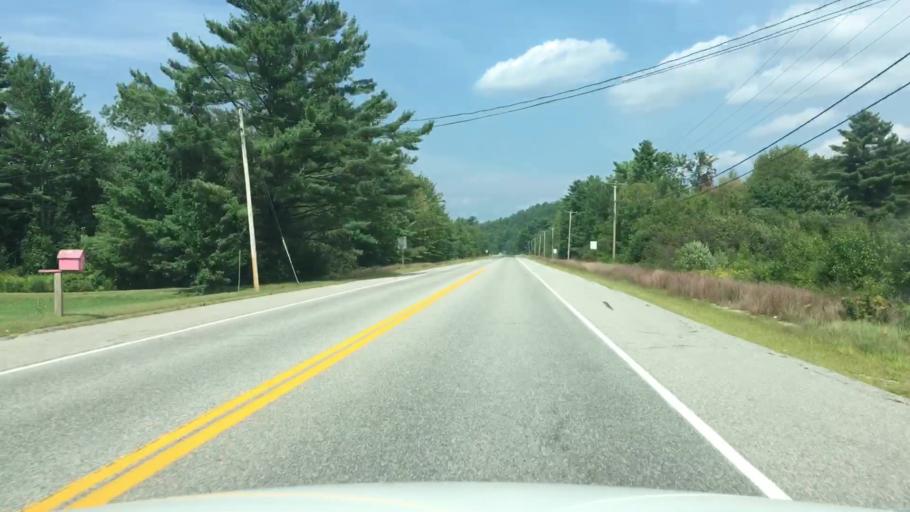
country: US
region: Maine
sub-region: Oxford County
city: Canton
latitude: 44.4469
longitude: -70.3170
